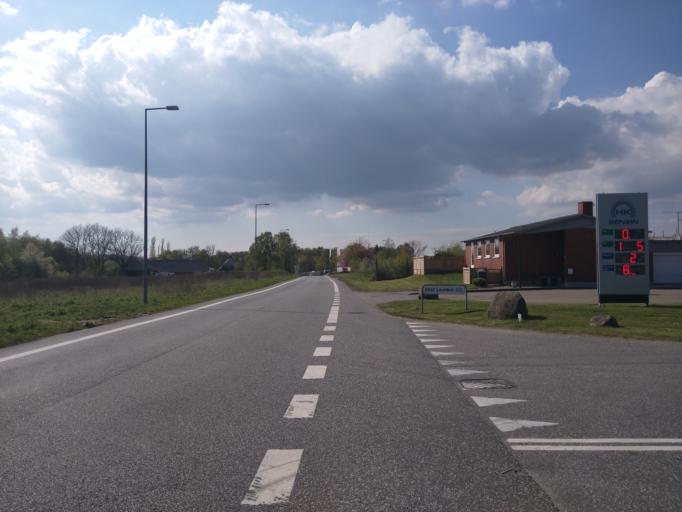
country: DK
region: South Denmark
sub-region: Fredericia Kommune
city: Snoghoj
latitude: 55.5431
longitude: 9.6886
